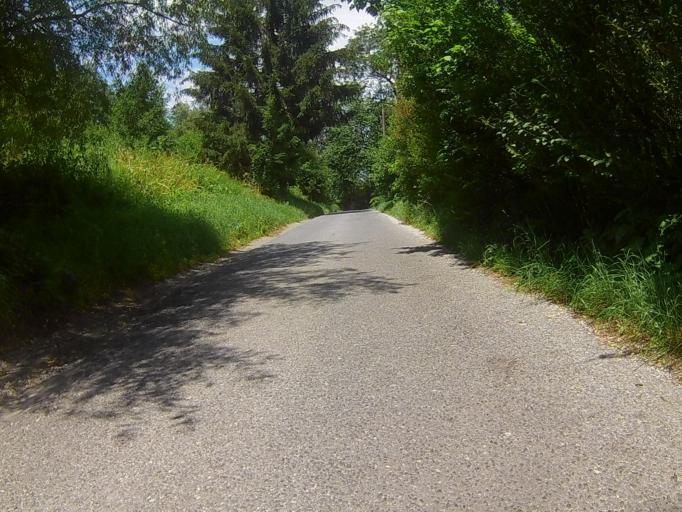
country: SI
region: Maribor
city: Kamnica
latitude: 46.5808
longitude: 15.6195
